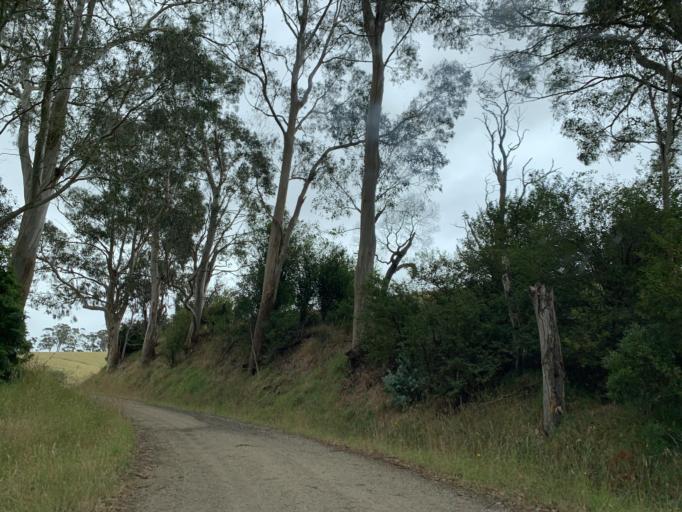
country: AU
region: Victoria
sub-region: Baw Baw
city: Warragul
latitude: -38.2874
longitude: 145.8745
